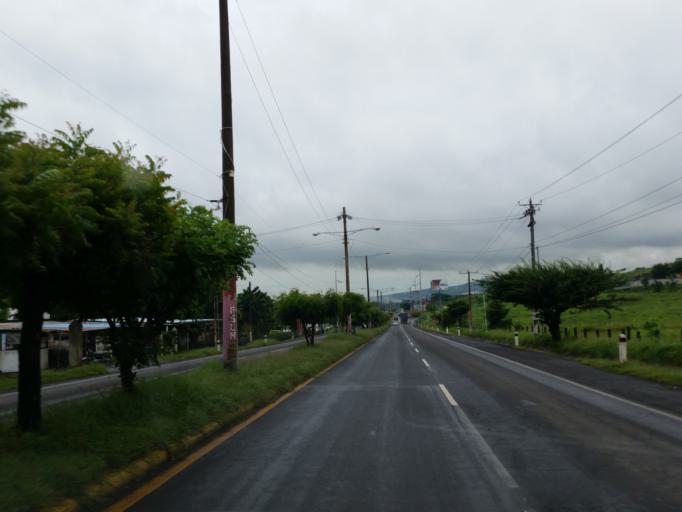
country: NI
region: Managua
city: Ciudad Sandino
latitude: 12.1513
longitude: -86.3369
